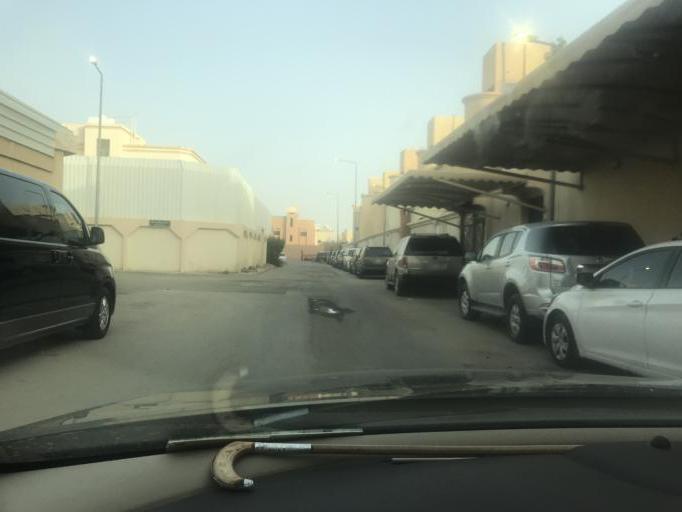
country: SA
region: Ar Riyad
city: Riyadh
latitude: 24.7452
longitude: 46.7795
